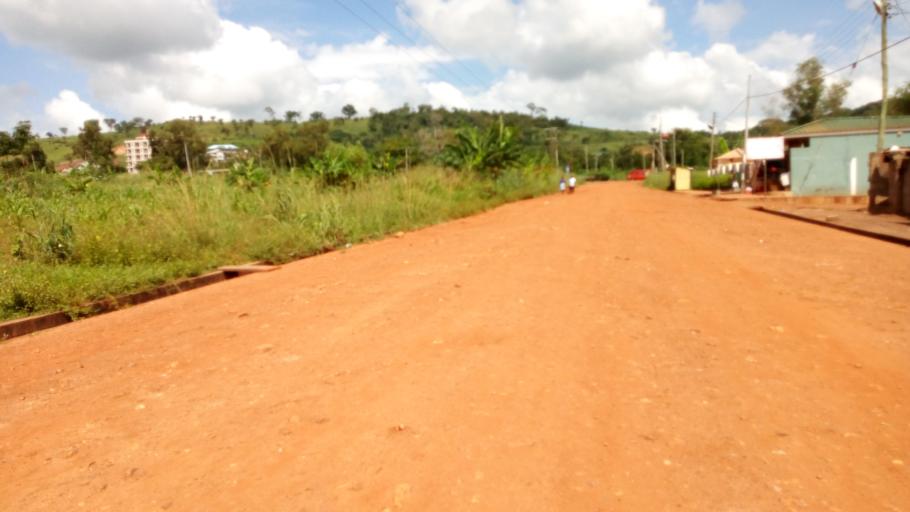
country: GH
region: Volta
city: Ho
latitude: 6.5933
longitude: 0.4403
